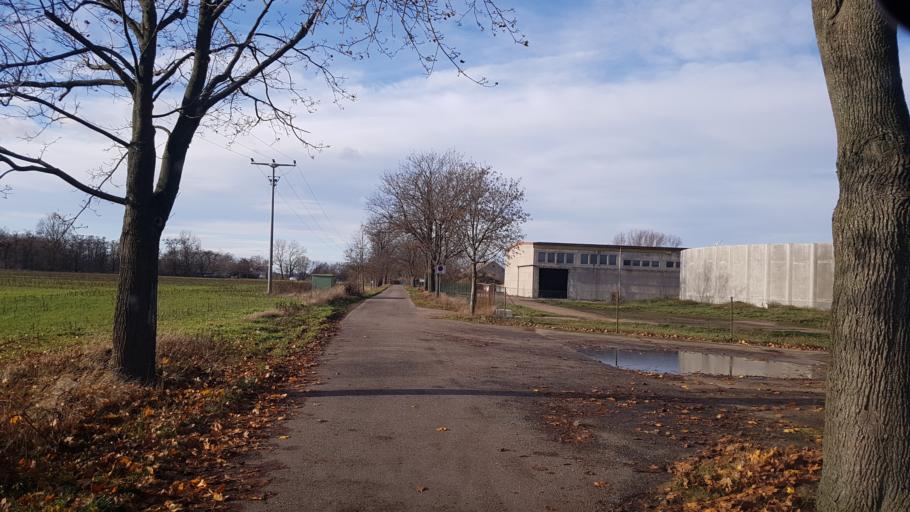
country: DE
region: Brandenburg
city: Falkenberg
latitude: 51.5949
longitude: 13.2694
